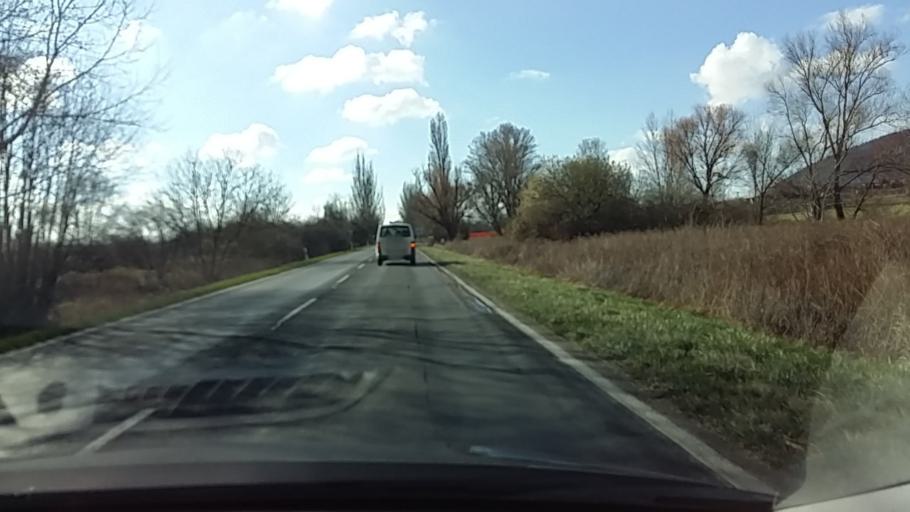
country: HU
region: Veszprem
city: Tapolca
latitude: 46.8219
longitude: 17.3807
